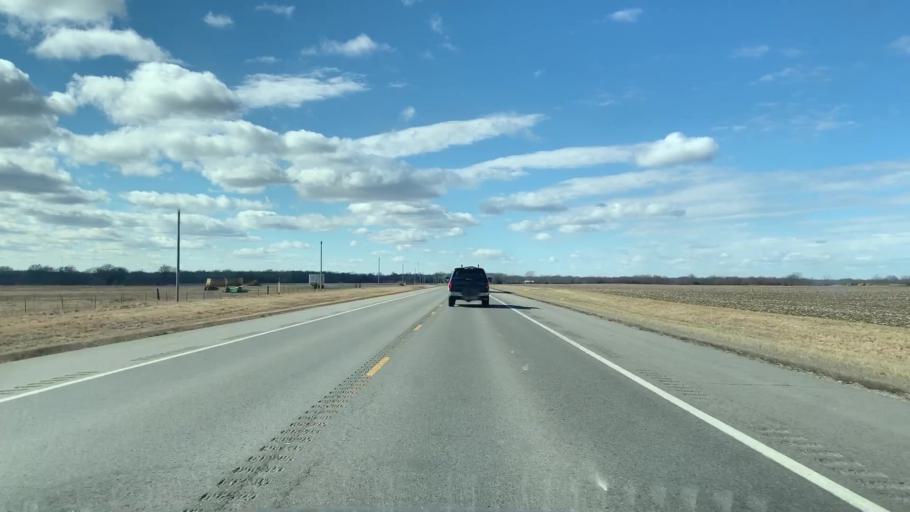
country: US
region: Kansas
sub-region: Cherokee County
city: Columbus
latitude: 37.3398
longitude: -94.8696
